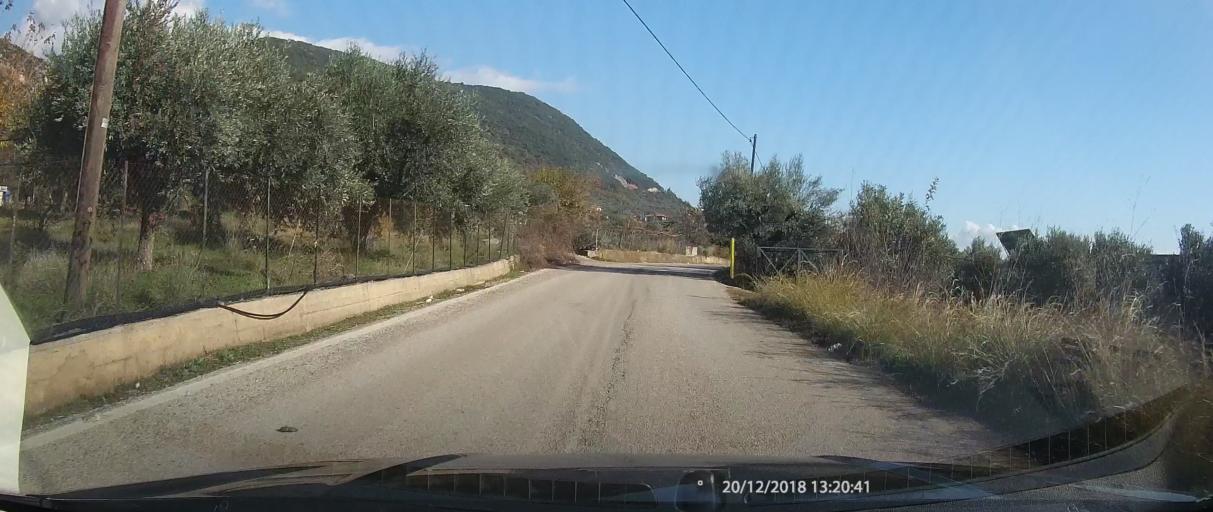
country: GR
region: West Greece
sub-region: Nomos Aitolias kai Akarnanias
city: Paravola
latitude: 38.6161
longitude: 21.5493
